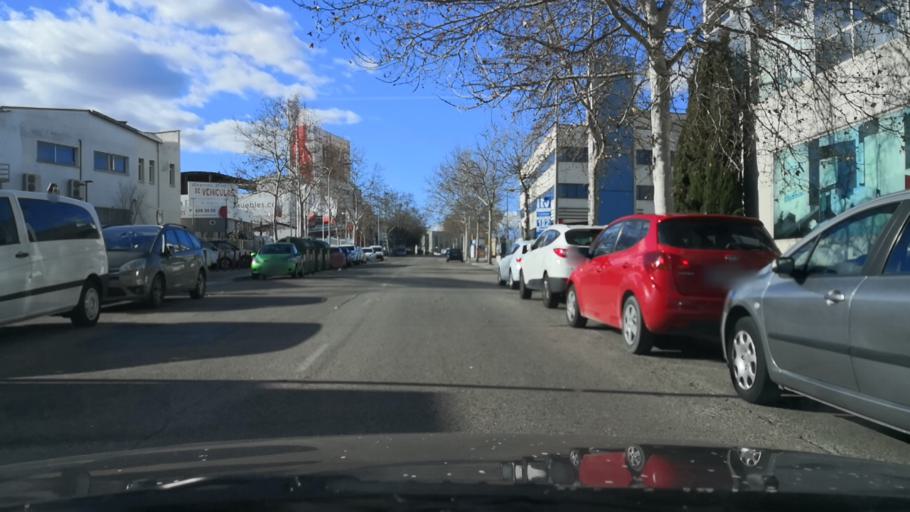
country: ES
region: Madrid
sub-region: Provincia de Madrid
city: San Sebastian de los Reyes
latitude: 40.5475
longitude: -3.6111
